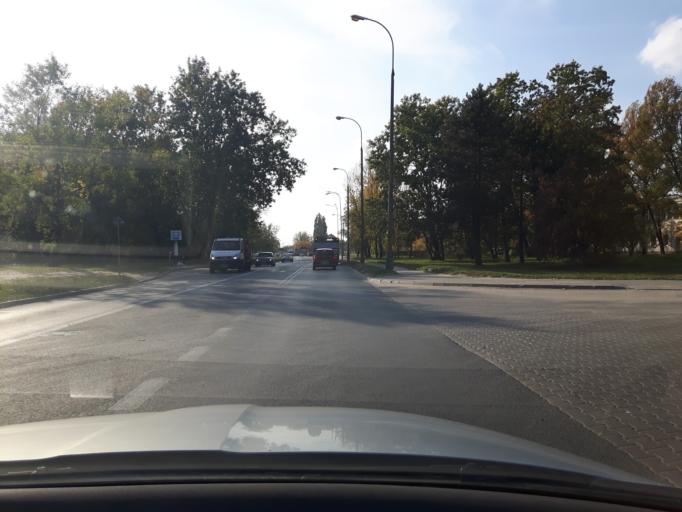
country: PL
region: Masovian Voivodeship
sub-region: Warszawa
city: Bialoleka
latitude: 52.3117
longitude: 20.9964
